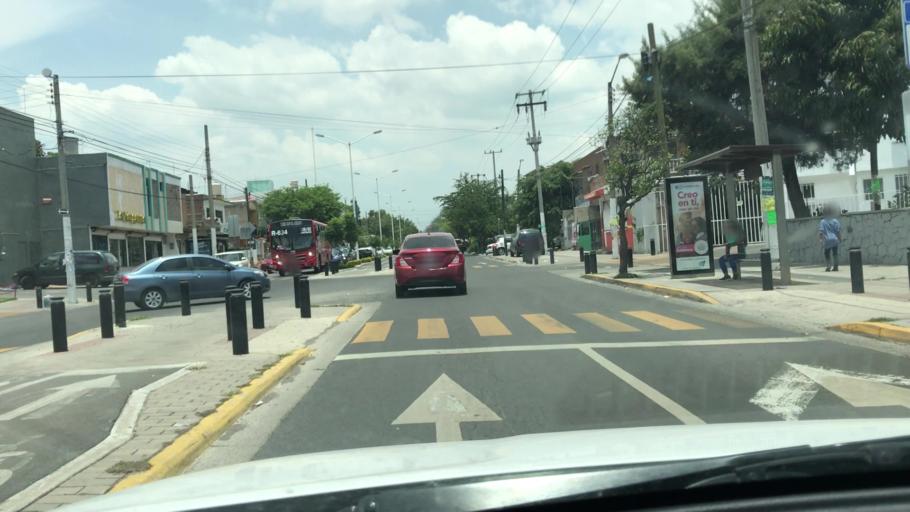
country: MX
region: Jalisco
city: Zapopan2
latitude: 20.7315
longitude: -103.4064
